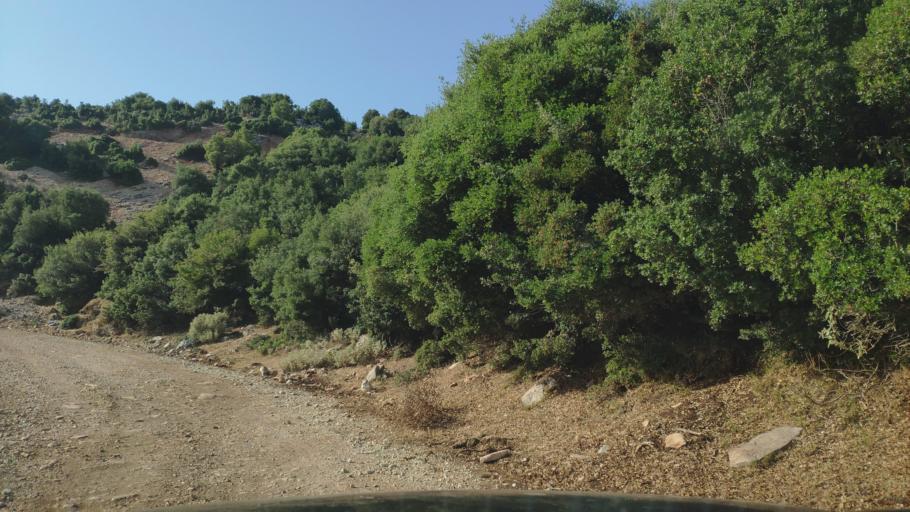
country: GR
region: West Greece
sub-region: Nomos Aitolias kai Akarnanias
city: Monastirakion
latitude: 38.8350
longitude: 20.9814
